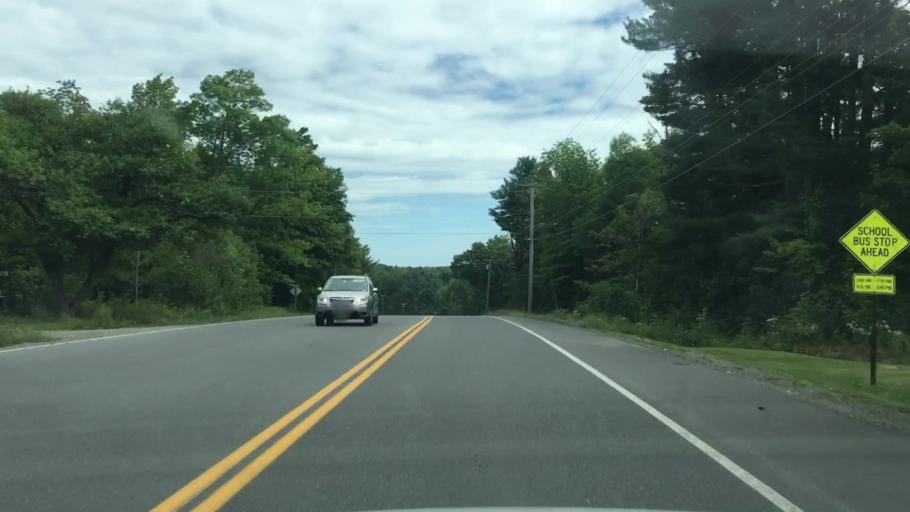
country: US
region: Maine
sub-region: Piscataquis County
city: Milo
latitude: 45.2367
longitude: -69.0544
